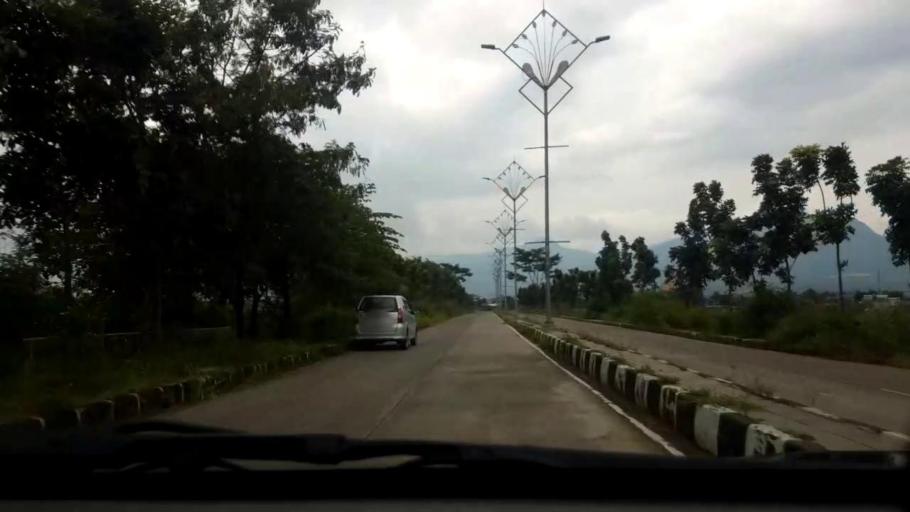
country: ID
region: West Java
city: Cileunyi
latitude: -6.9523
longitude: 107.7110
